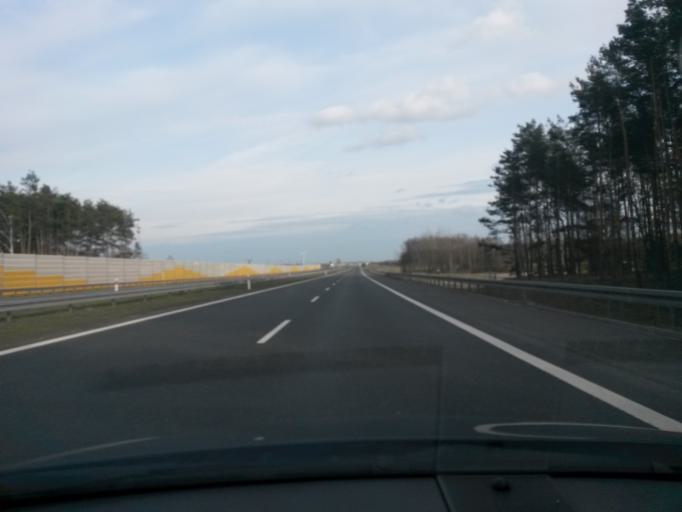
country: PL
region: Lodz Voivodeship
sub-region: Powiat leczycki
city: Swinice Warckie
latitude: 52.0246
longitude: 18.9203
